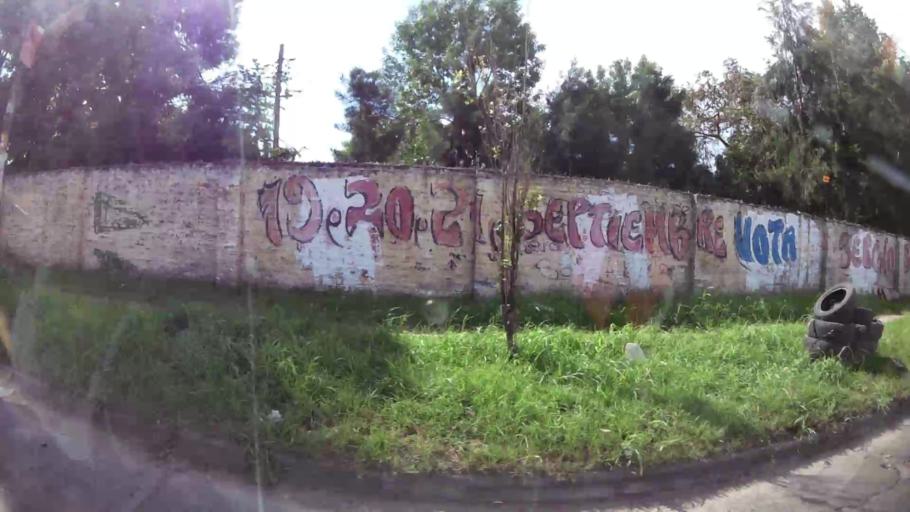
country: AR
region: Buenos Aires
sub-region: Partido de Merlo
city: Merlo
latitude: -34.6381
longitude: -58.7139
